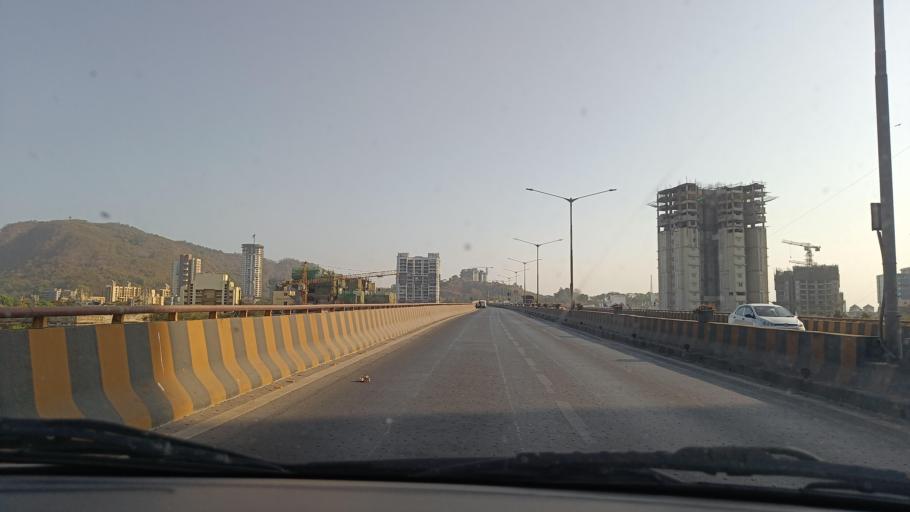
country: IN
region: Maharashtra
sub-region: Mumbai Suburban
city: Mumbai
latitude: 19.0498
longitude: 72.9104
